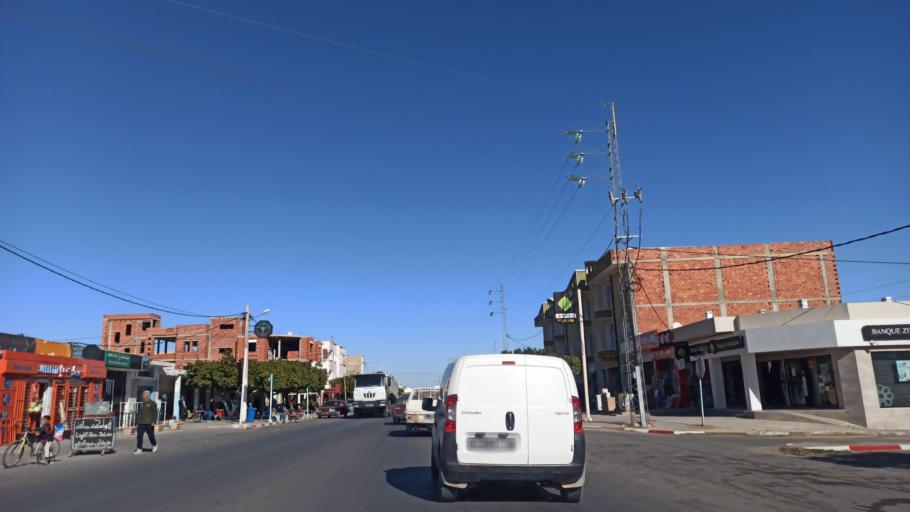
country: TN
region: Sidi Bu Zayd
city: Bi'r al Hufayy
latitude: 34.9274
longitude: 9.1922
